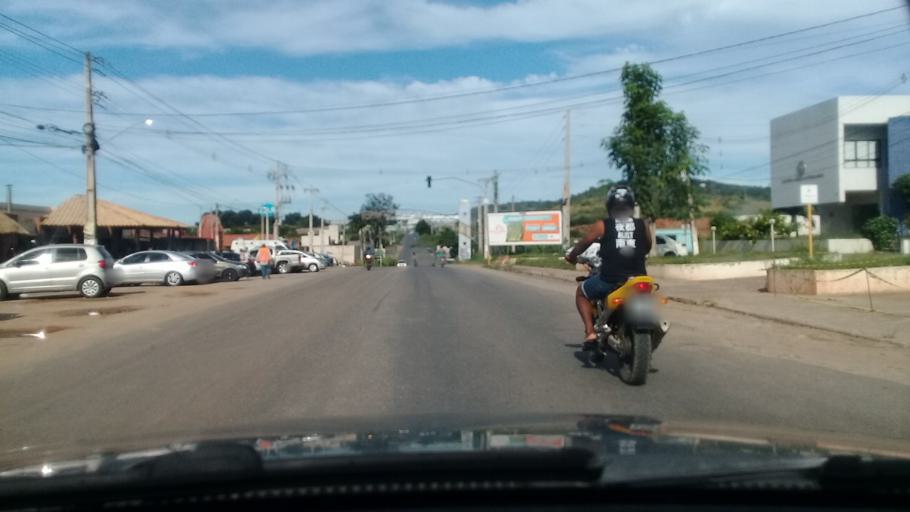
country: BR
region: Pernambuco
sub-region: Vitoria De Santo Antao
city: Vitoria de Santo Antao
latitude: -8.1157
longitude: -35.2702
